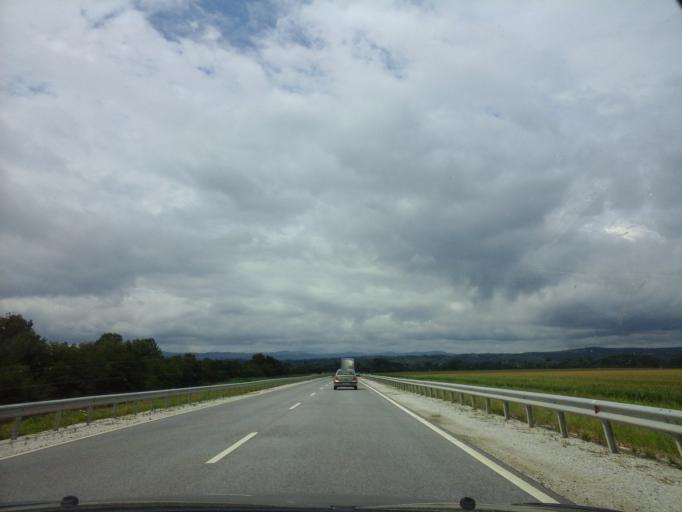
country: HU
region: Borsod-Abauj-Zemplen
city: Szirmabesenyo
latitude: 48.1360
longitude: 20.8251
